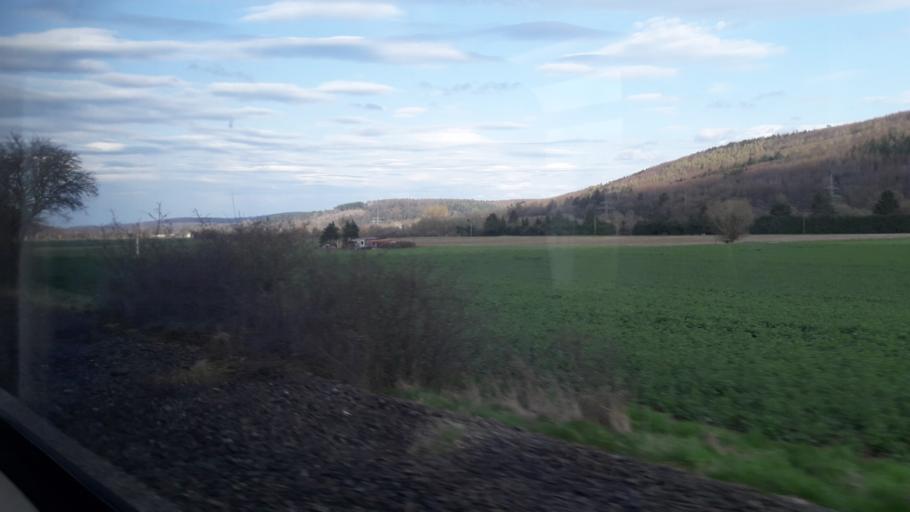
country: DE
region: North Rhine-Westphalia
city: Marsberg
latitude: 51.5003
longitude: 8.9282
